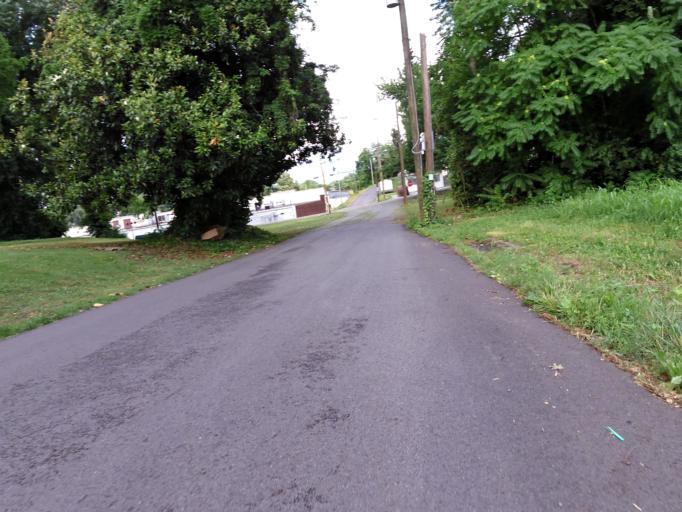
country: US
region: Tennessee
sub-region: Knox County
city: Knoxville
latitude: 35.9909
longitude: -83.9237
